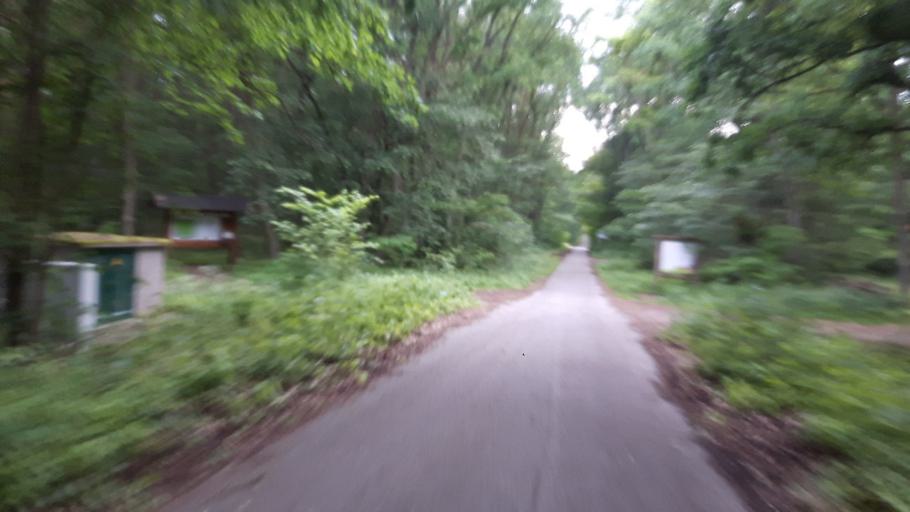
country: PL
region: West Pomeranian Voivodeship
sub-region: Powiat gryfinski
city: Widuchowa
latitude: 53.1328
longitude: 14.3471
